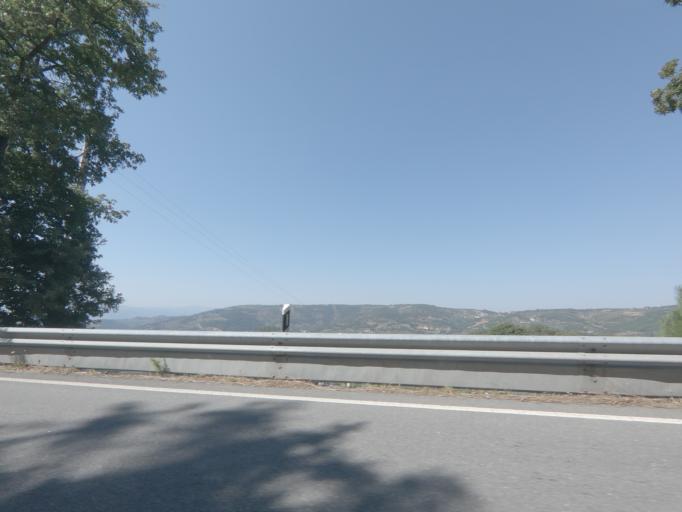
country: PT
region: Viseu
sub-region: Tarouca
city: Tarouca
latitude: 41.0393
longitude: -7.7358
